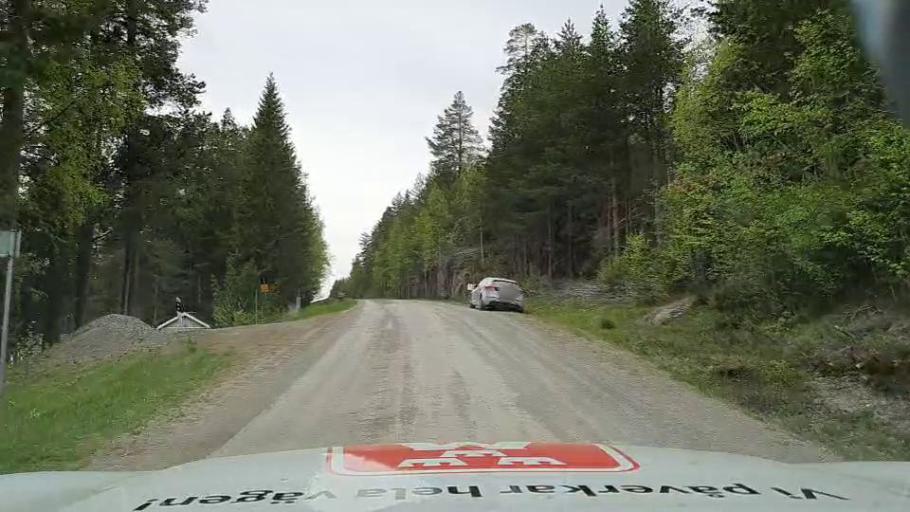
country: SE
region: Jaemtland
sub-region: Bergs Kommun
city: Hoverberg
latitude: 62.7207
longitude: 14.6750
